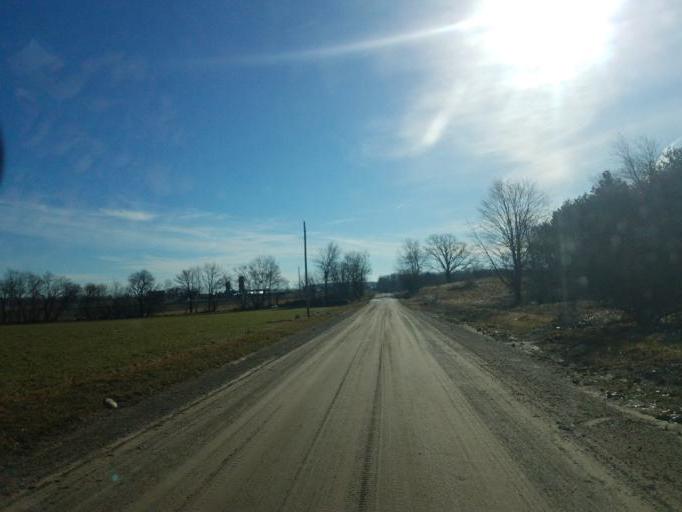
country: US
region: Michigan
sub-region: Montcalm County
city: Edmore
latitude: 43.4949
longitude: -85.0723
